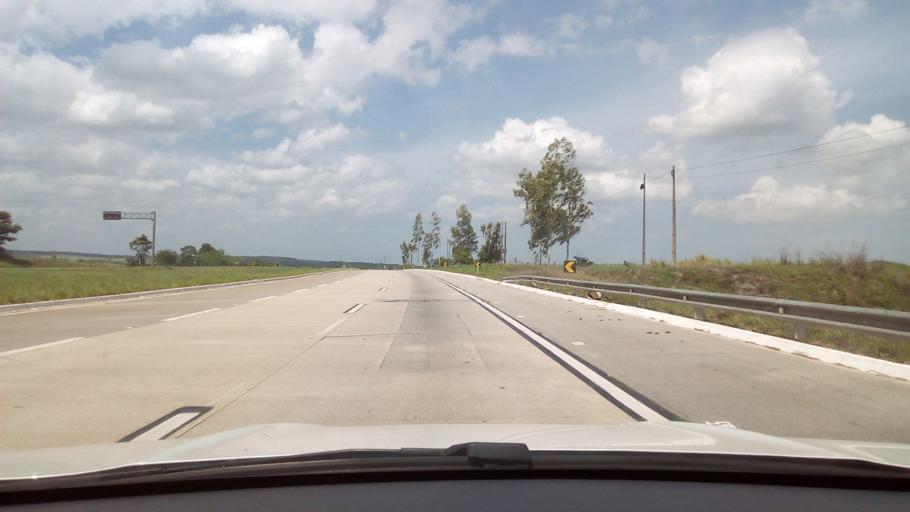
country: BR
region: Paraiba
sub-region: Mamanguape
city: Mamanguape
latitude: -6.7869
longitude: -35.1343
